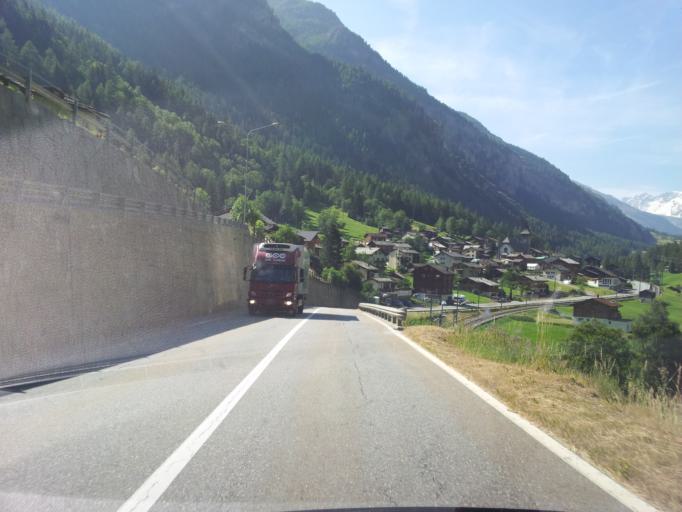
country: CH
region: Valais
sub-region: Visp District
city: Sankt Niklaus
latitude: 46.1394
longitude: 7.7916
